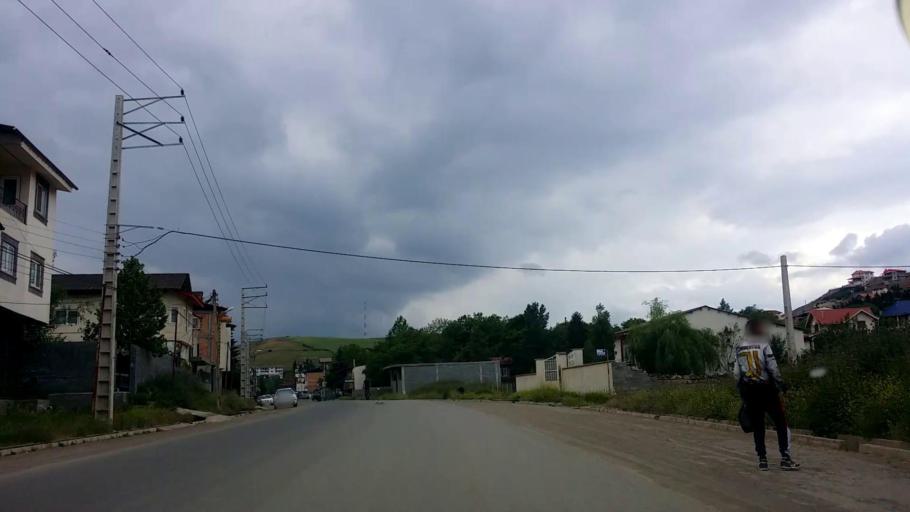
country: IR
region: Mazandaran
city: Chalus
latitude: 36.5130
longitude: 51.2552
